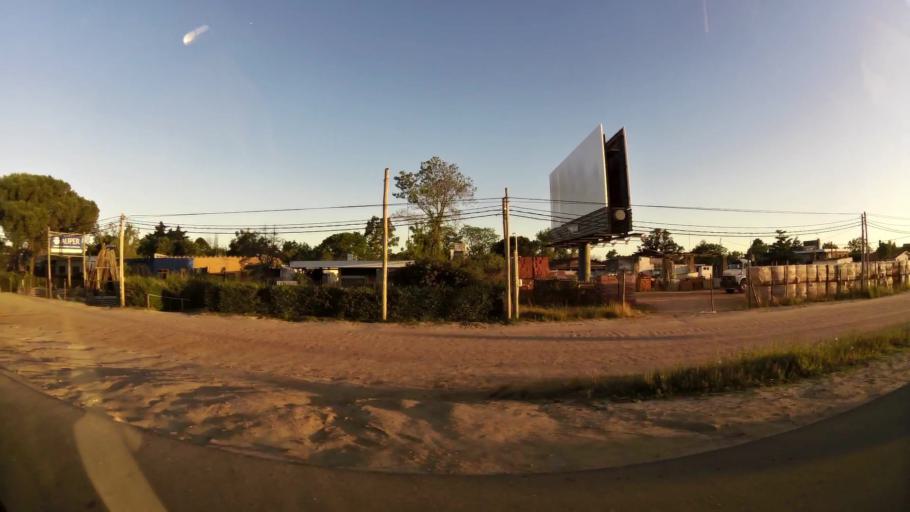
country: UY
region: Canelones
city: Barra de Carrasco
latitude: -34.8431
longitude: -55.9968
